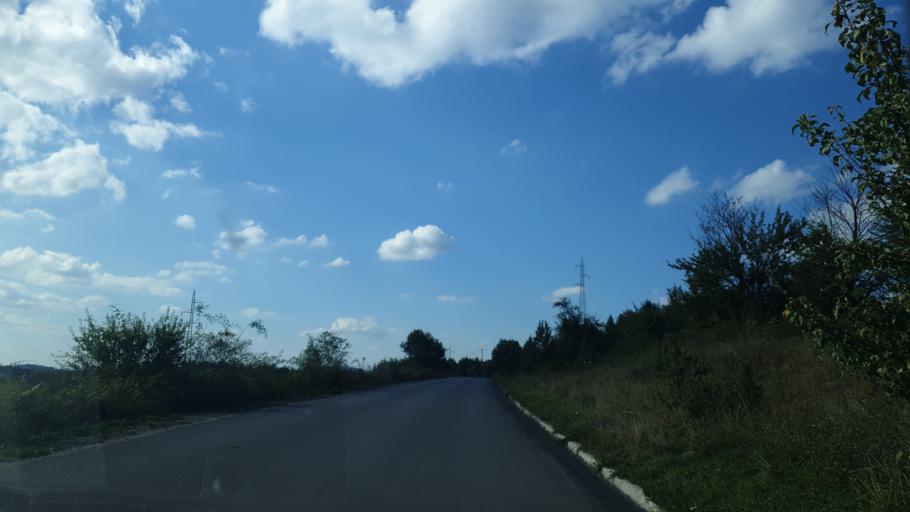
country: RS
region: Central Serbia
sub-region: Zlatiborski Okrug
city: Nova Varos
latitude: 43.4276
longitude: 19.8965
